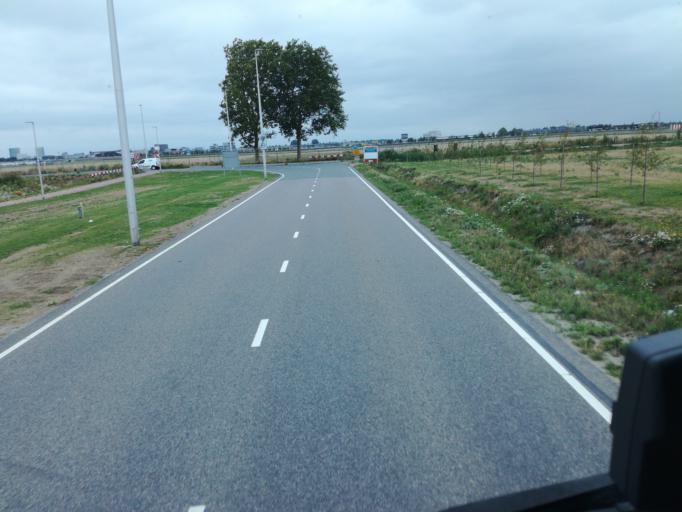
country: NL
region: North Holland
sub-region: Gemeente Aalsmeer
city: Aalsmeer
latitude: 52.2853
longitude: 4.7449
